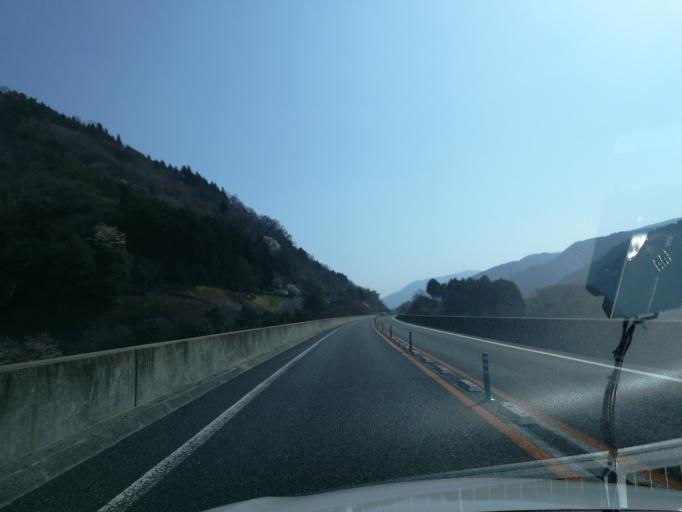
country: JP
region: Tokushima
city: Ikedacho
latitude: 34.0110
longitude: 133.7310
